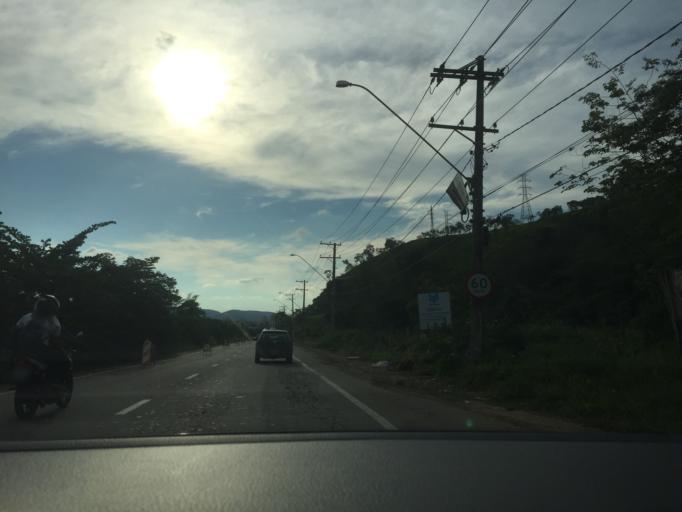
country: BR
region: Sao Paulo
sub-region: Varzea Paulista
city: Varzea Paulista
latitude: -23.2015
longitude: -46.8451
